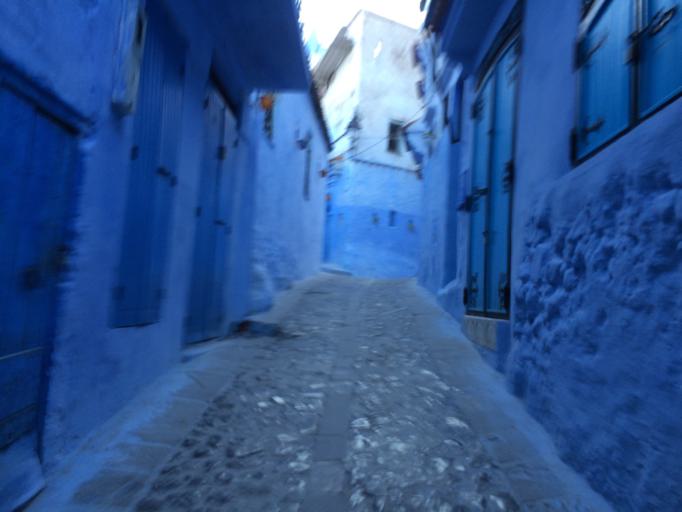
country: MA
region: Tanger-Tetouan
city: Chefchaouene
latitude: 35.1701
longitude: -5.2599
